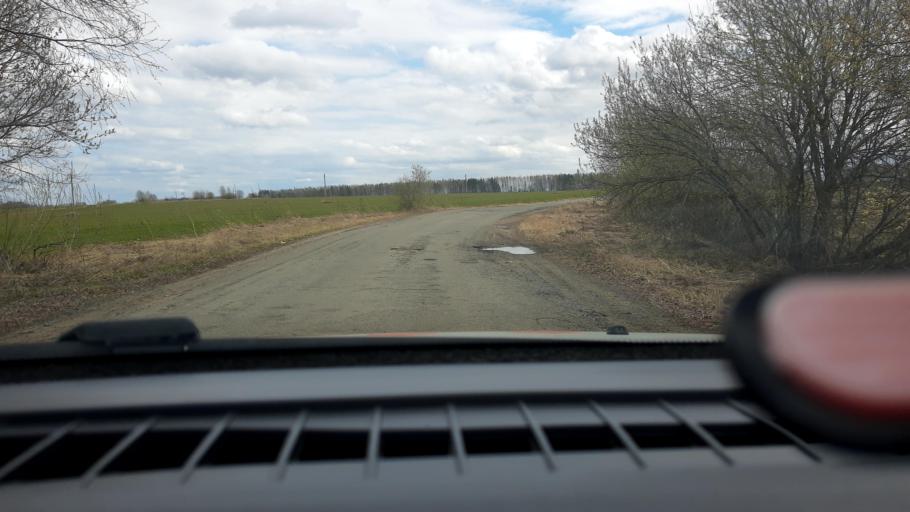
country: RU
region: Nizjnij Novgorod
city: Burevestnik
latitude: 56.1615
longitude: 43.6948
